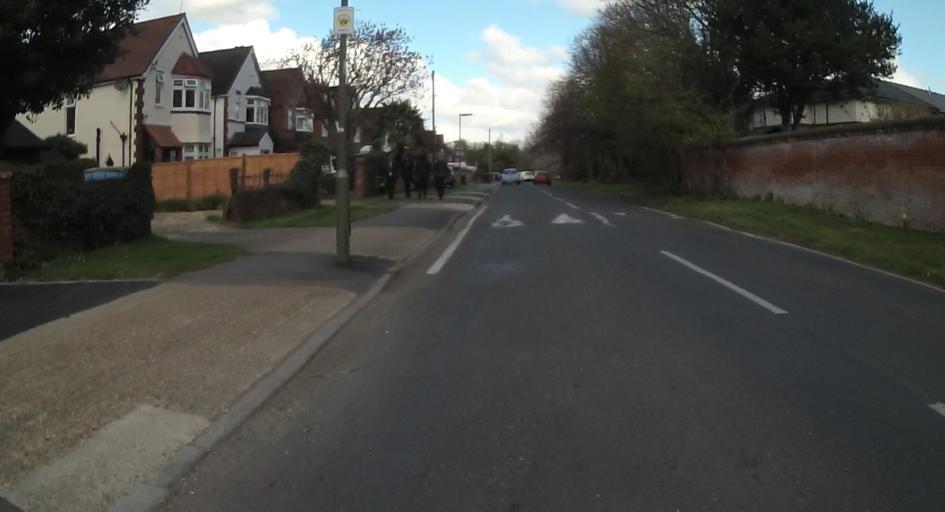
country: GB
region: England
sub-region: Surrey
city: Addlestone
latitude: 51.3734
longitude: -0.5022
